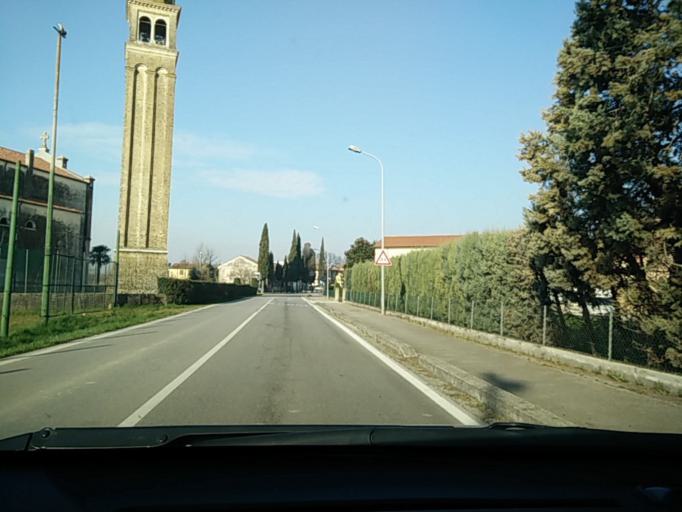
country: IT
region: Veneto
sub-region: Provincia di Treviso
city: Pero
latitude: 45.7040
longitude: 12.3527
